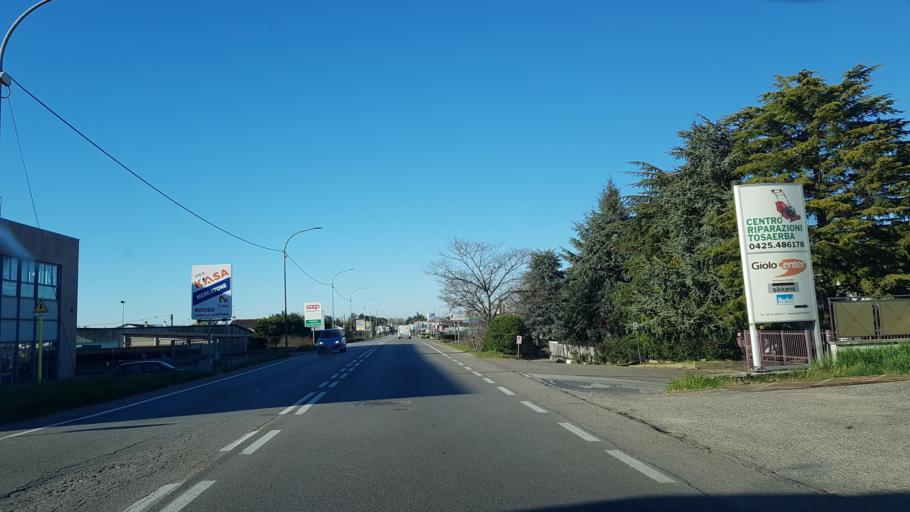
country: IT
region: Veneto
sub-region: Provincia di Padova
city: Boara Pisani
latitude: 45.0966
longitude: 11.7856
